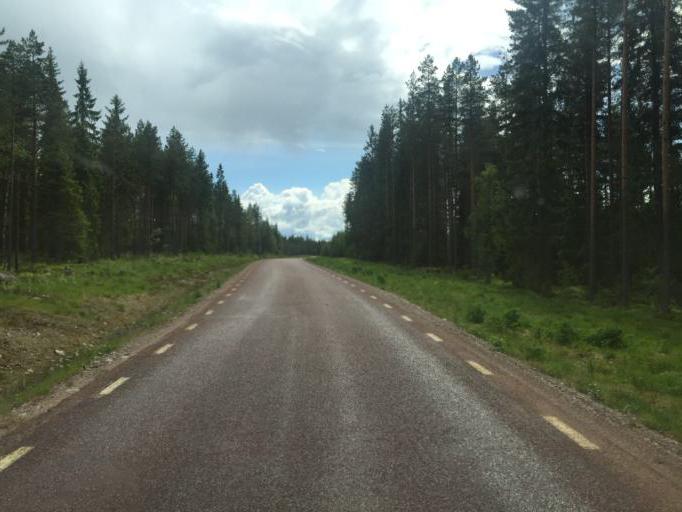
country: SE
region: Dalarna
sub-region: Malung-Saelens kommun
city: Malung
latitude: 60.3556
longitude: 13.8661
